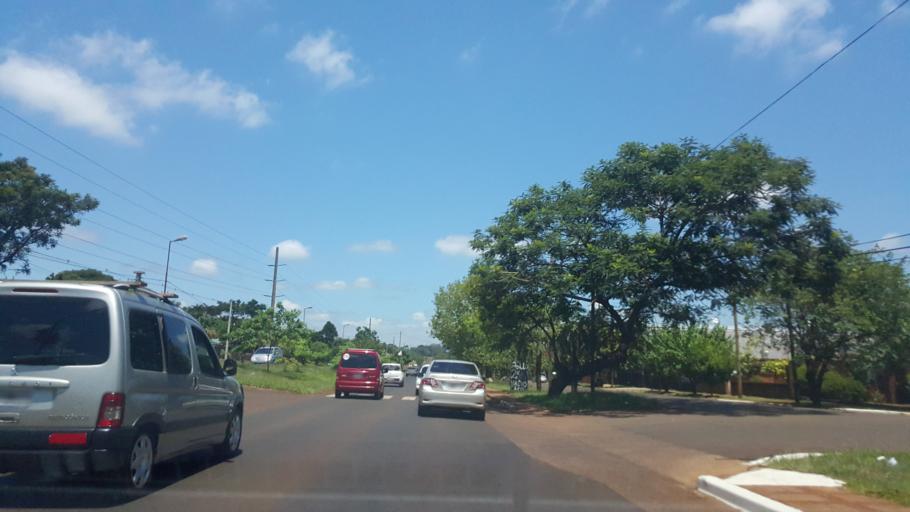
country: AR
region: Misiones
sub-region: Departamento de Capital
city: Posadas
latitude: -27.4151
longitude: -55.9286
